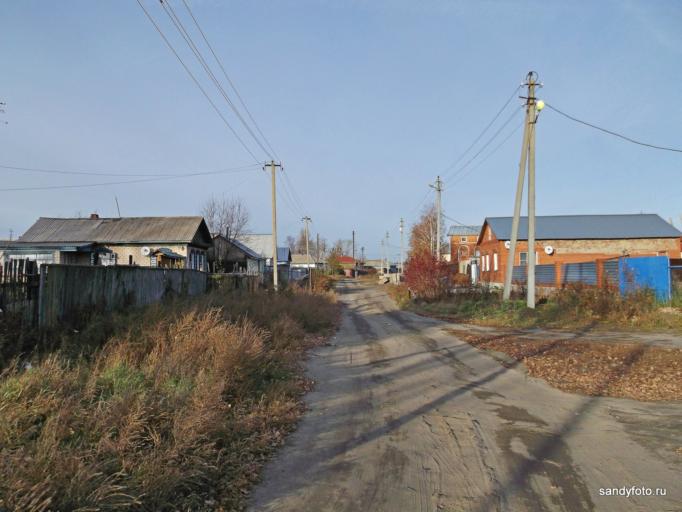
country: RU
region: Chelyabinsk
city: Troitsk
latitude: 54.0722
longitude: 61.5858
